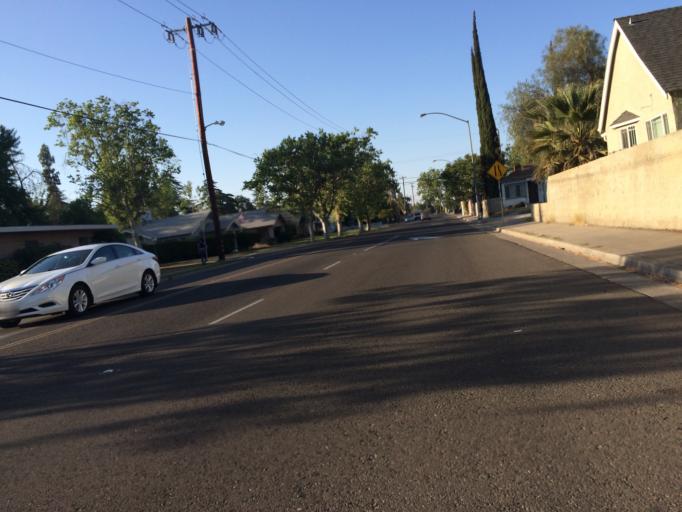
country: US
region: California
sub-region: Fresno County
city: Fresno
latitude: 36.7808
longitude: -119.7996
